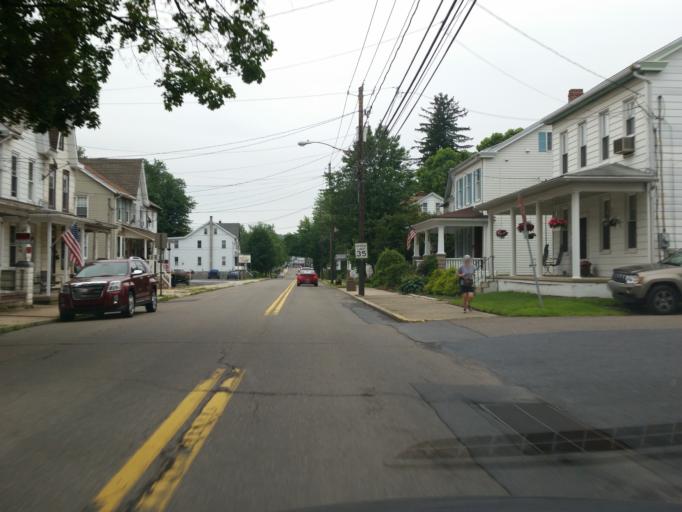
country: US
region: Pennsylvania
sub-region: Schuylkill County
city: Pine Grove
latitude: 40.5557
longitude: -76.3905
